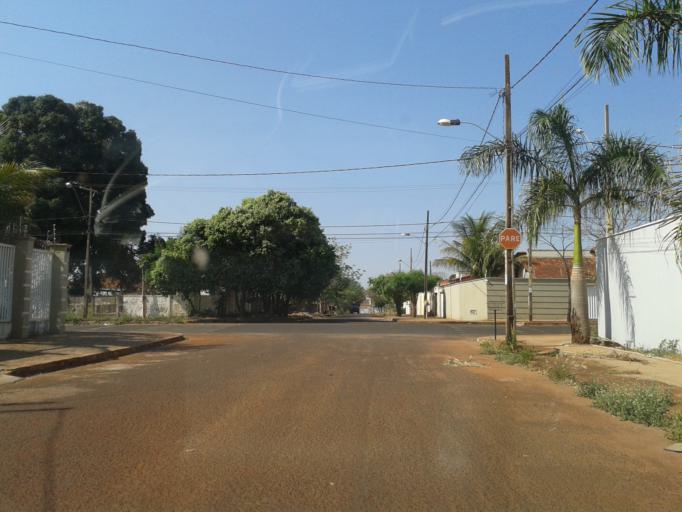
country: BR
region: Minas Gerais
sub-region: Ituiutaba
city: Ituiutaba
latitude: -18.9703
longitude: -49.4455
